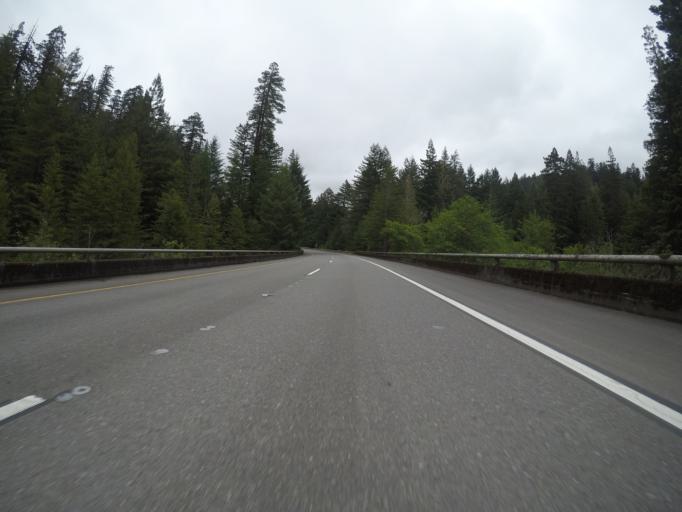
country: US
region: California
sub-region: Humboldt County
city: Rio Dell
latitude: 40.4406
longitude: -124.0376
